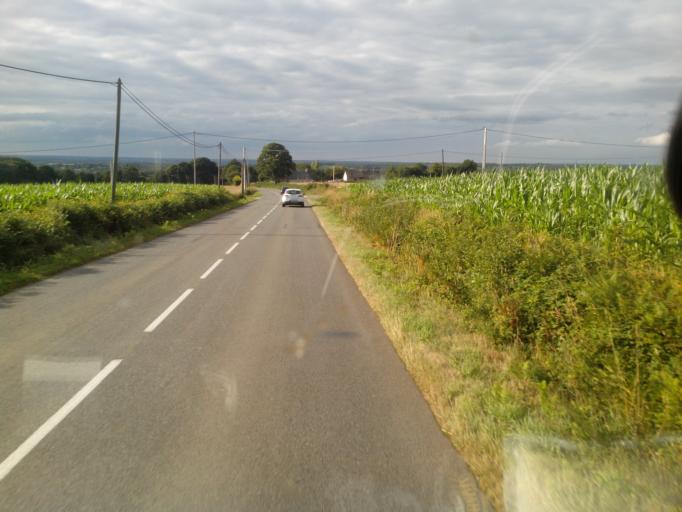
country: FR
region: Brittany
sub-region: Departement d'Ille-et-Vilaine
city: Paimpont
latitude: 48.0426
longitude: -2.1837
